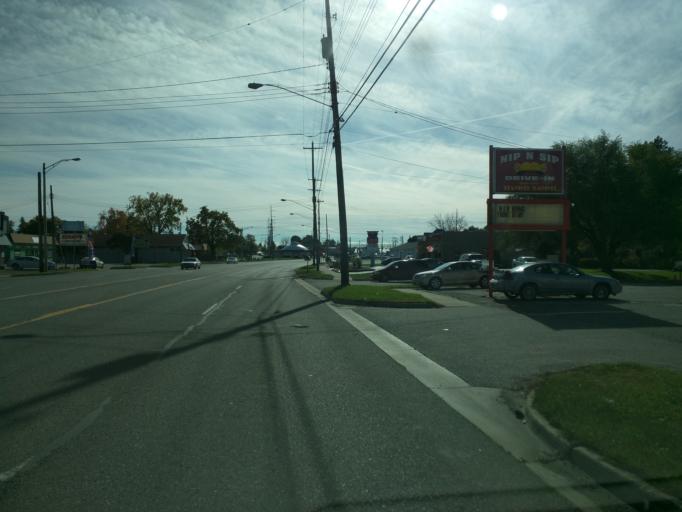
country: US
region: Michigan
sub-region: Ingham County
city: Lansing
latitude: 42.7607
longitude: -84.5429
